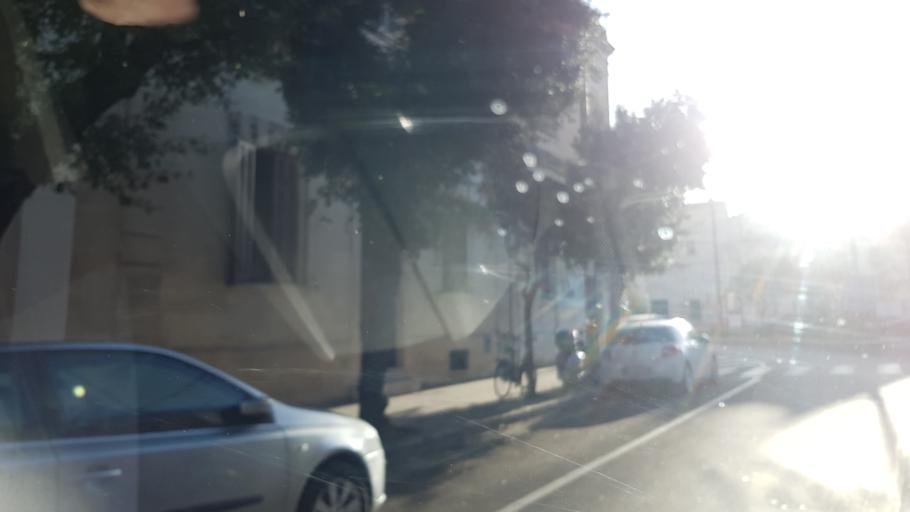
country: IT
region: Apulia
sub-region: Provincia di Lecce
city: Lecce
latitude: 40.3500
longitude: 18.1622
